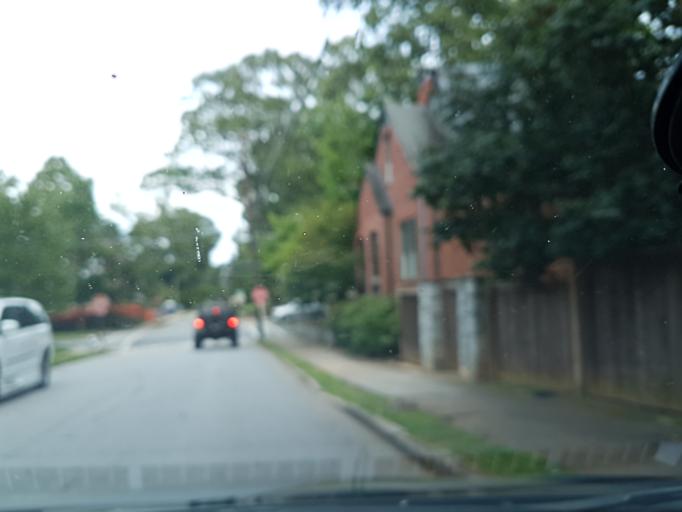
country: US
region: Georgia
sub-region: DeKalb County
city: Druid Hills
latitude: 33.7876
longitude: -84.3504
